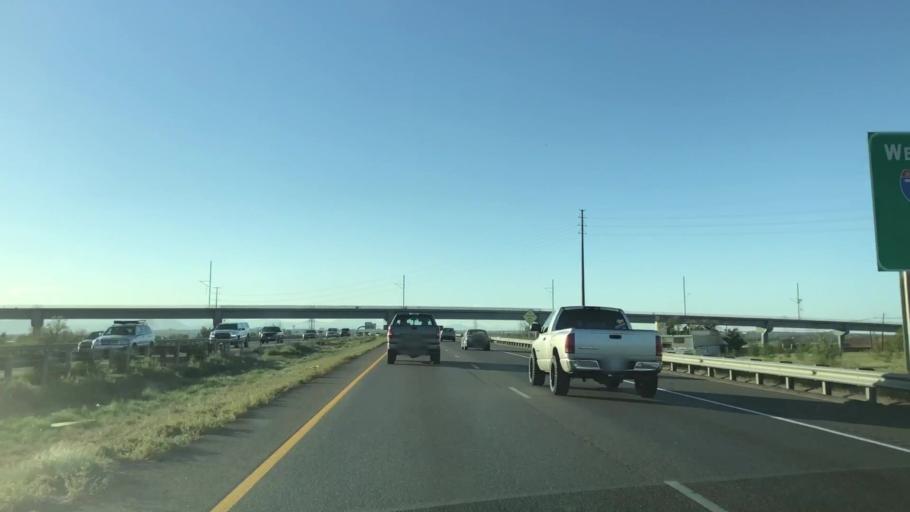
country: US
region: Colorado
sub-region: Adams County
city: Commerce City
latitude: 39.8106
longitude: -104.9468
